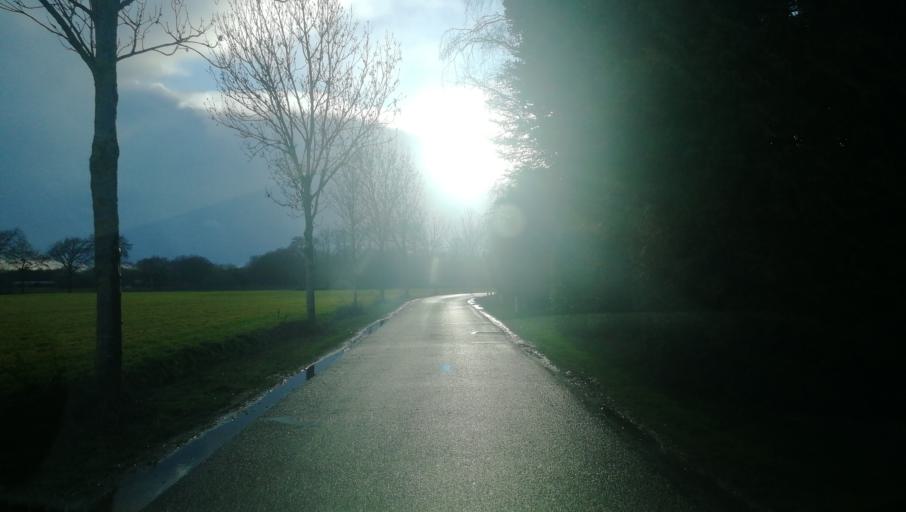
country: NL
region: Limburg
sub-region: Gemeente Peel en Maas
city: Maasbree
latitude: 51.3504
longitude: 6.0436
